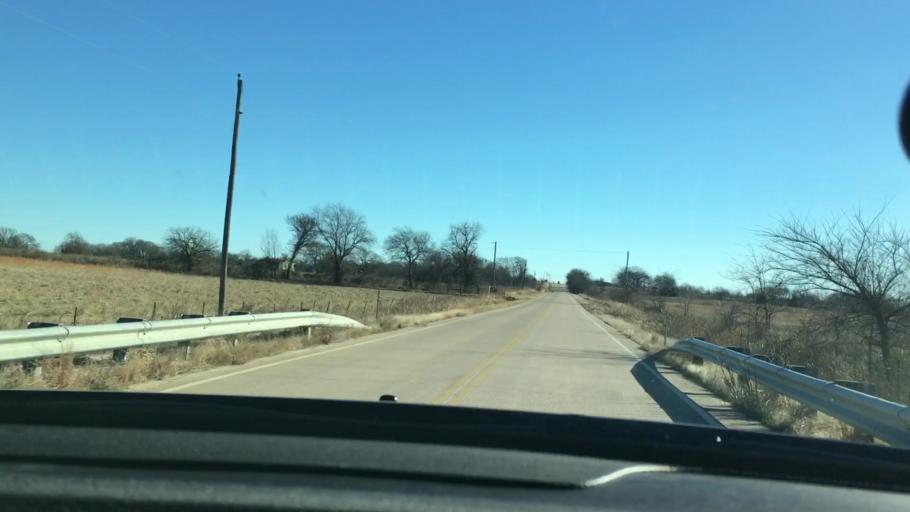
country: US
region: Oklahoma
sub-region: Marshall County
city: Madill
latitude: 34.1144
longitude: -96.7163
